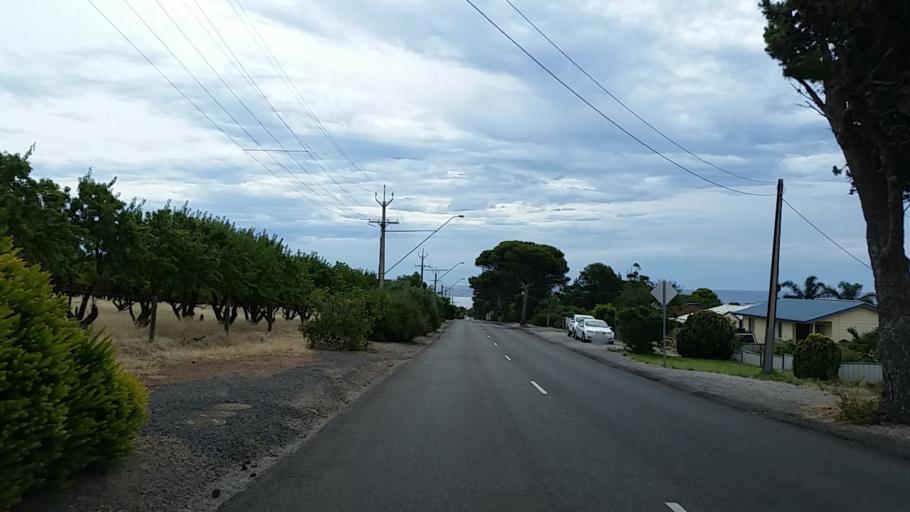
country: AU
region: South Australia
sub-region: Onkaparinga
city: Aldinga
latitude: -35.3286
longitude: 138.4728
